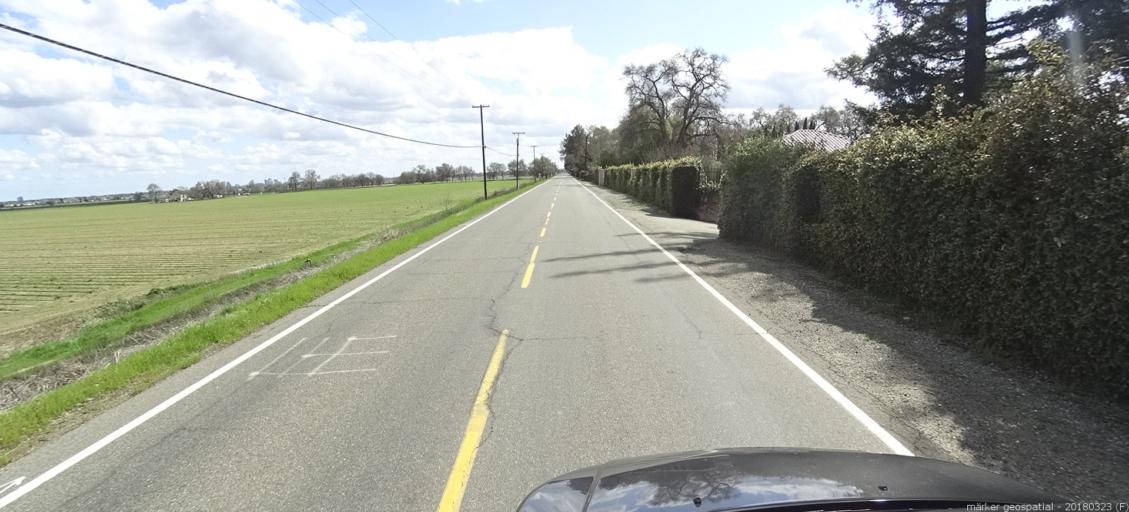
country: US
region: California
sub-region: Yolo County
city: West Sacramento
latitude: 38.6396
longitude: -121.5624
